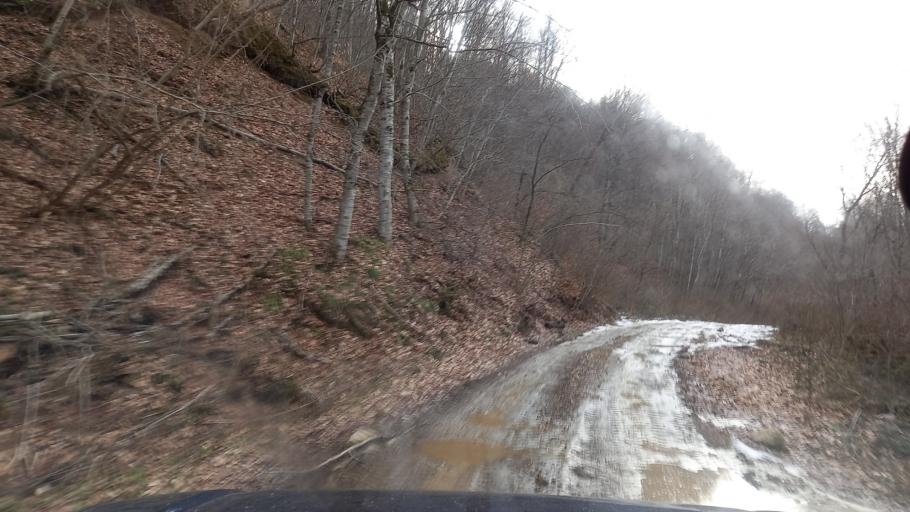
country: RU
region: Adygeya
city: Kamennomostskiy
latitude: 44.1541
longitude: 40.3027
